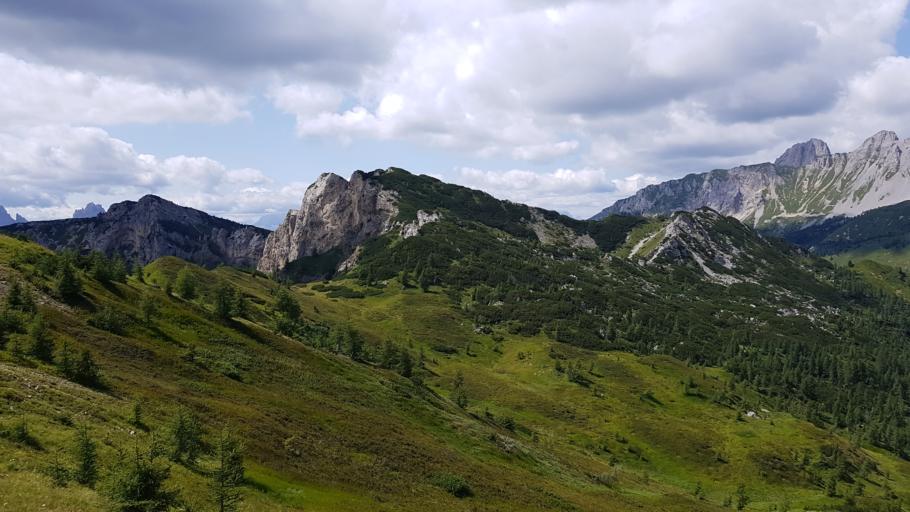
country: IT
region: Friuli Venezia Giulia
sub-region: Provincia di Udine
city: Vico
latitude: 46.4455
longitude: 12.6249
